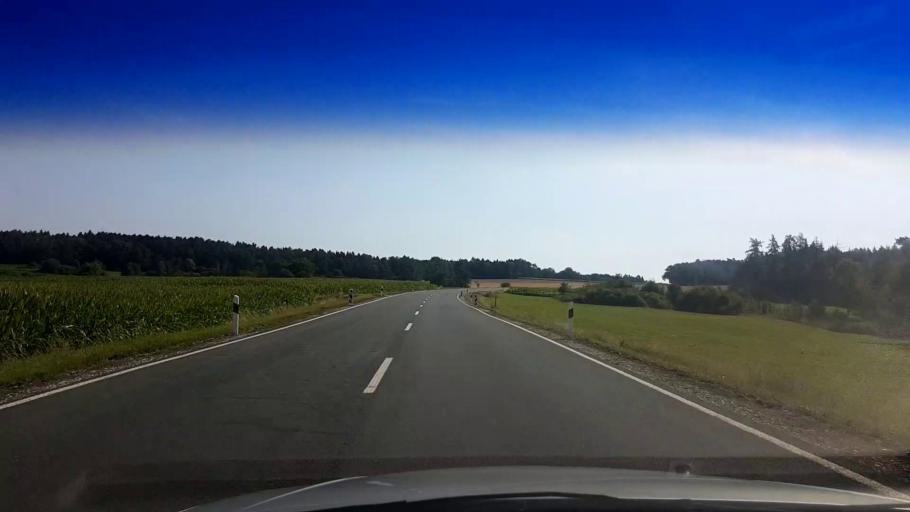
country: DE
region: Bavaria
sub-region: Upper Franconia
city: Hollfeld
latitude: 49.9455
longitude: 11.3123
